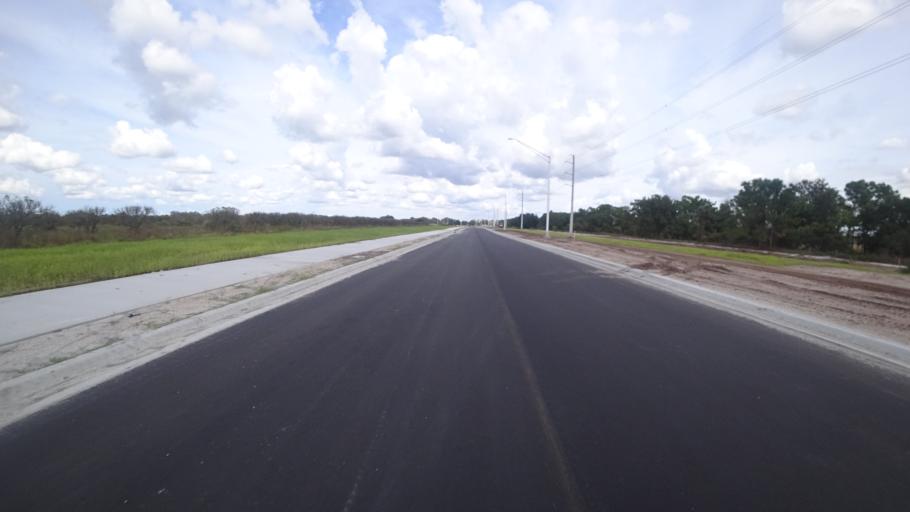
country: US
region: Florida
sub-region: Sarasota County
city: The Meadows
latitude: 27.4692
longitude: -82.3510
